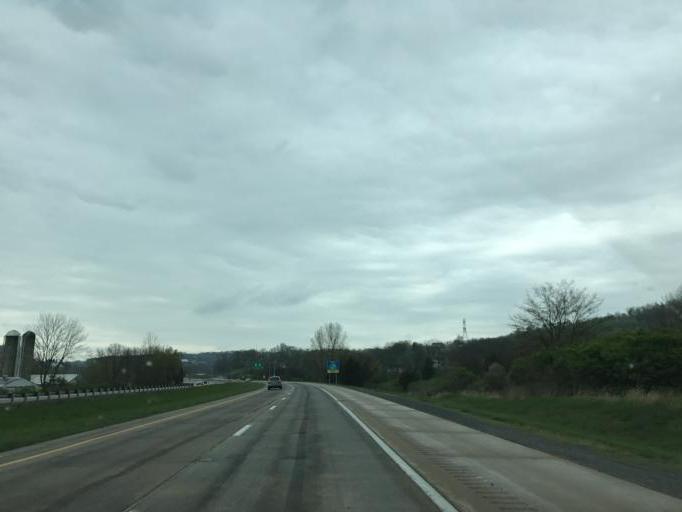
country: US
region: Pennsylvania
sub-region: Lancaster County
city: Adamstown
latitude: 40.2408
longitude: -76.0404
